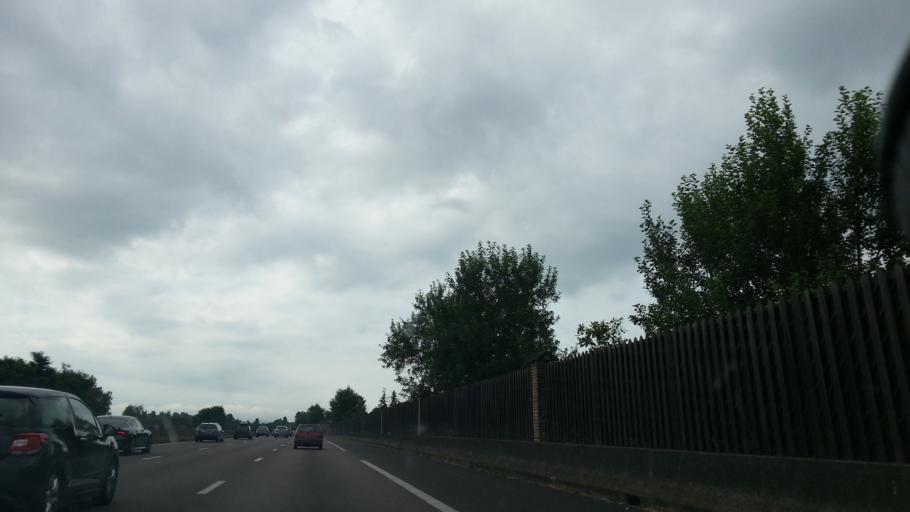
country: FR
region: Bourgogne
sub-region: Departement de Saone-et-Loire
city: Chatenoy-le-Royal
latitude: 46.7772
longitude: 4.8193
